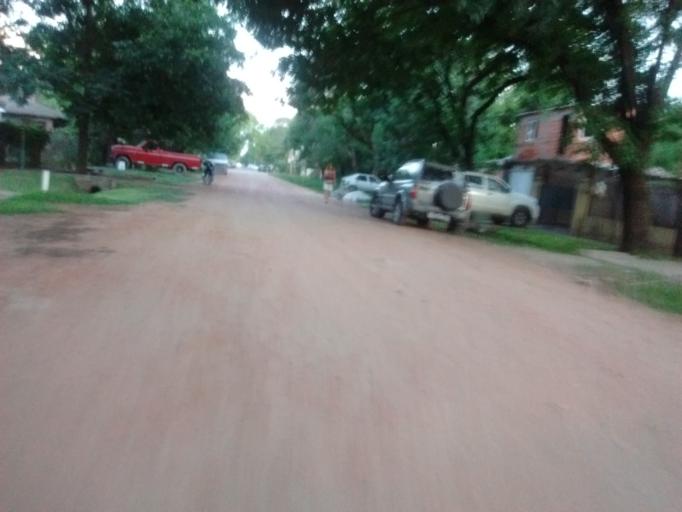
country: AR
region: Santa Fe
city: Funes
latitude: -32.9099
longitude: -60.8122
